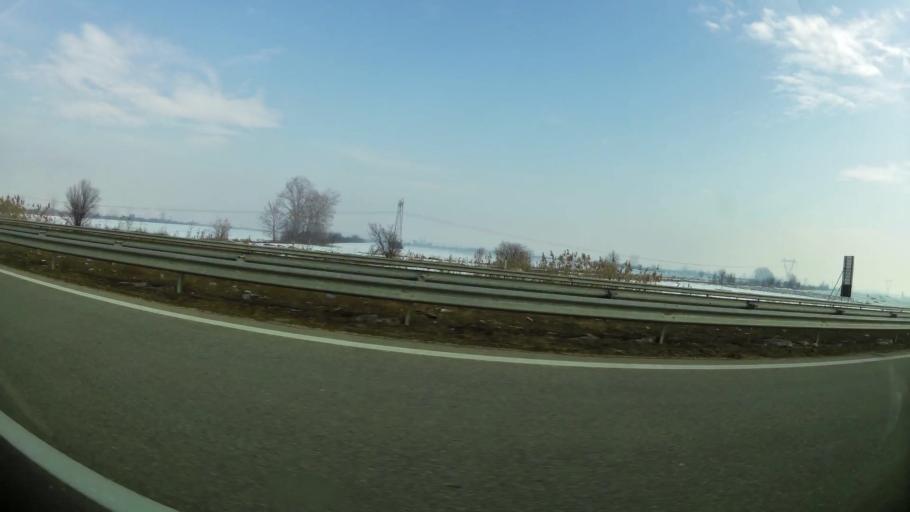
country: MK
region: Aracinovo
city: Arachinovo
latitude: 42.0109
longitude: 21.5346
